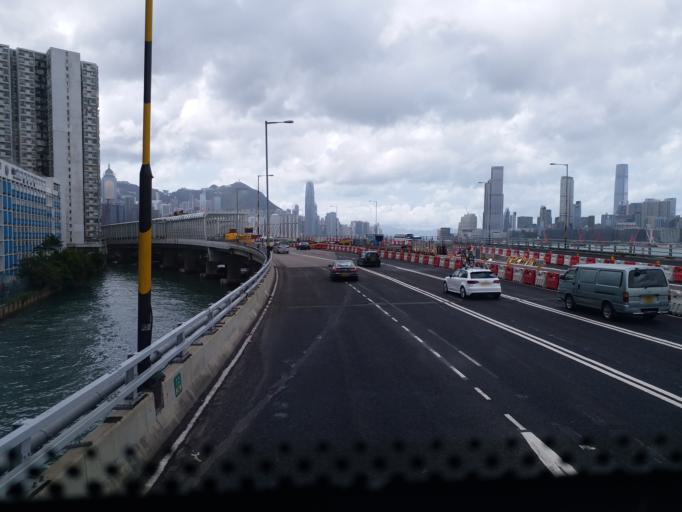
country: HK
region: Wanchai
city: Wan Chai
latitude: 22.2928
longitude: 114.1958
